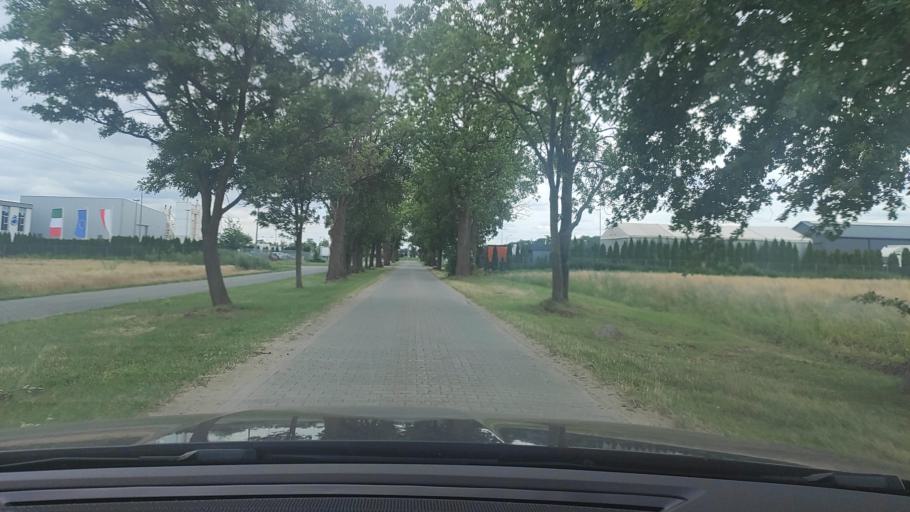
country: PL
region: Greater Poland Voivodeship
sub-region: Powiat poznanski
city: Swarzedz
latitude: 52.3785
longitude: 17.1099
